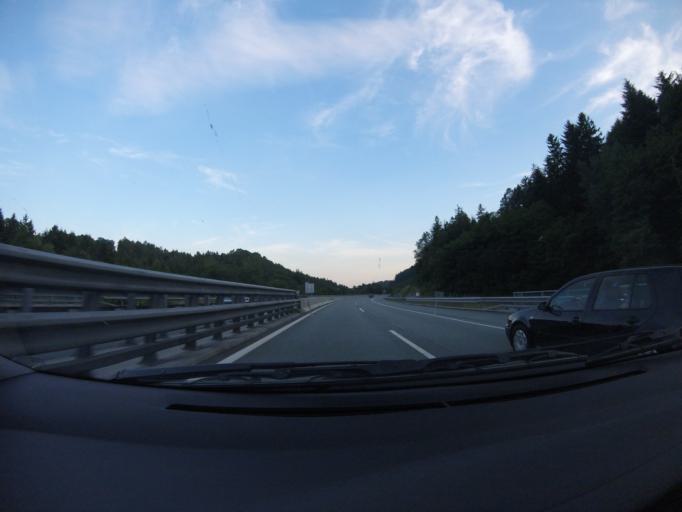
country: AT
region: Styria
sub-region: Politischer Bezirk Hartberg-Fuerstenfeld
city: Schaeffern
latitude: 47.4702
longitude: 16.0974
